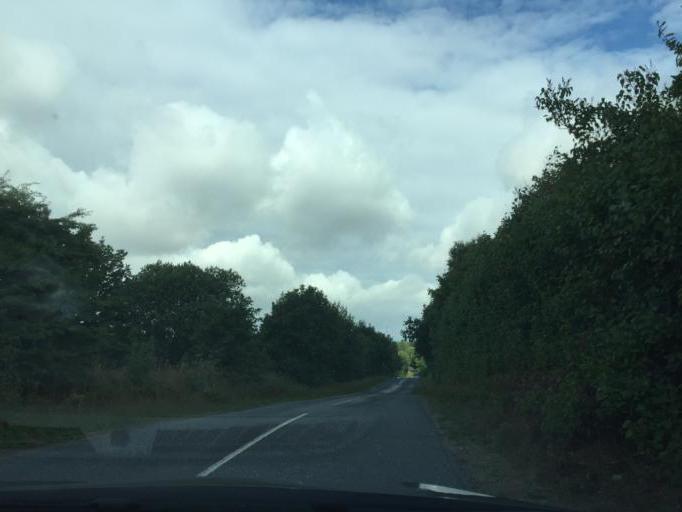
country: DK
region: South Denmark
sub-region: Assens Kommune
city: Harby
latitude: 55.1996
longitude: 10.1787
